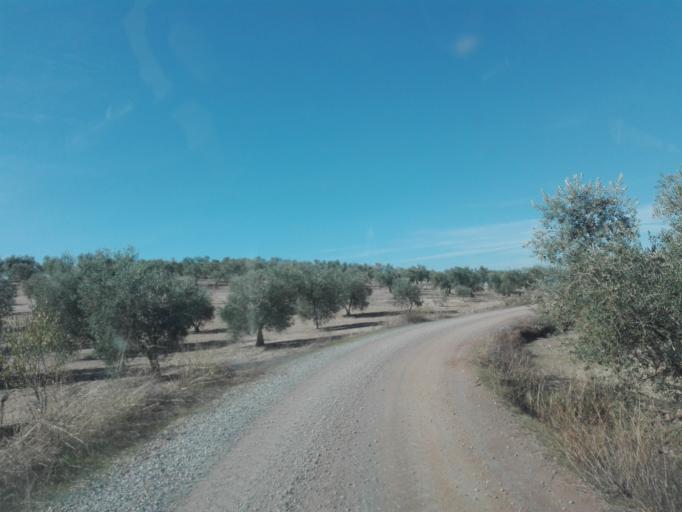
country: ES
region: Extremadura
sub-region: Provincia de Badajoz
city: Ahillones
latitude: 38.2818
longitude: -5.9102
